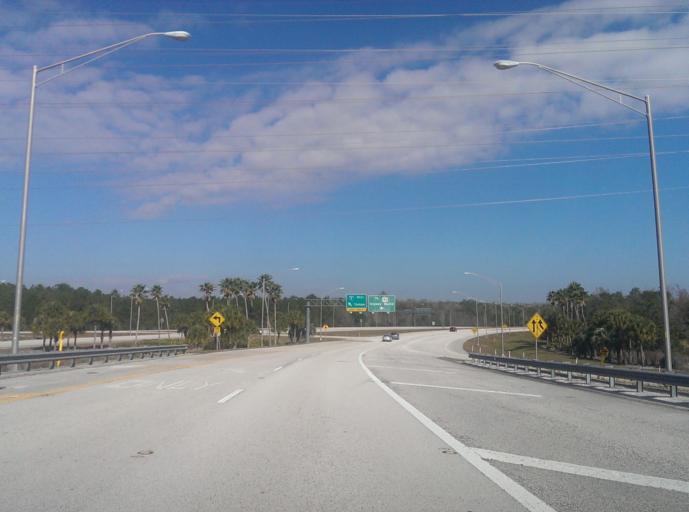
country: US
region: Florida
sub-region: Osceola County
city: Celebration
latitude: 28.3084
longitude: -81.5713
